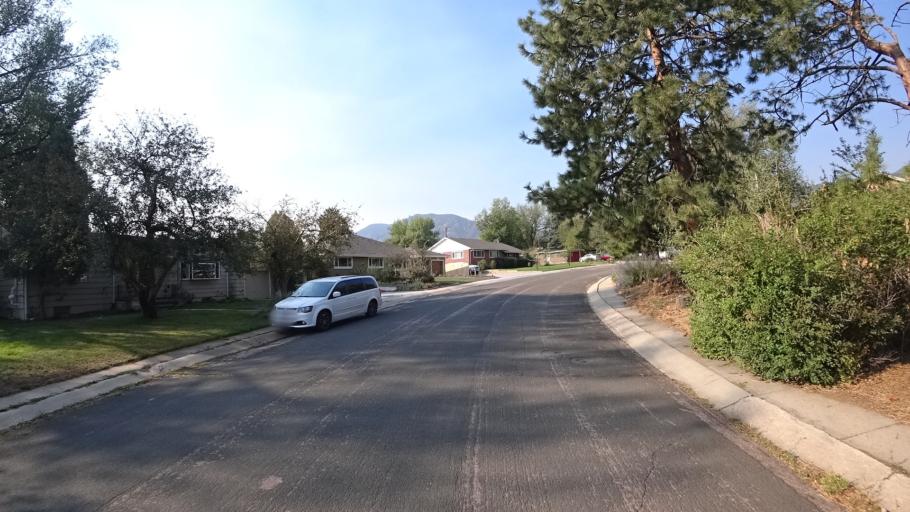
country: US
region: Colorado
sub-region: El Paso County
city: Colorado Springs
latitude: 38.8051
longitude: -104.8484
